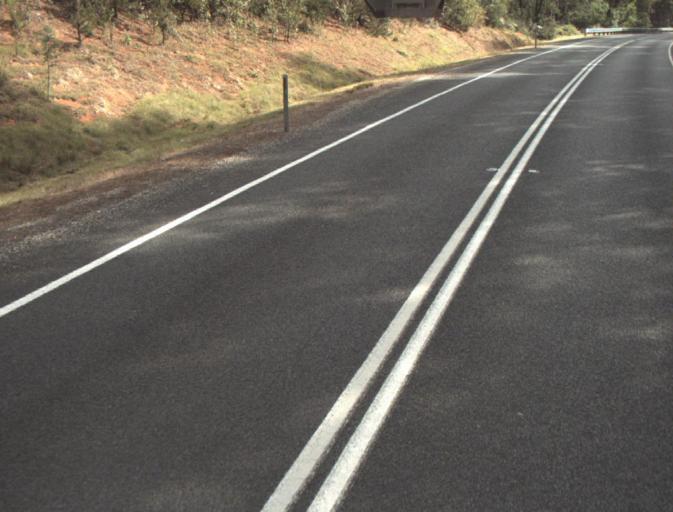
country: AU
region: Tasmania
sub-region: Launceston
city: Mayfield
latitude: -41.3009
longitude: 147.2064
